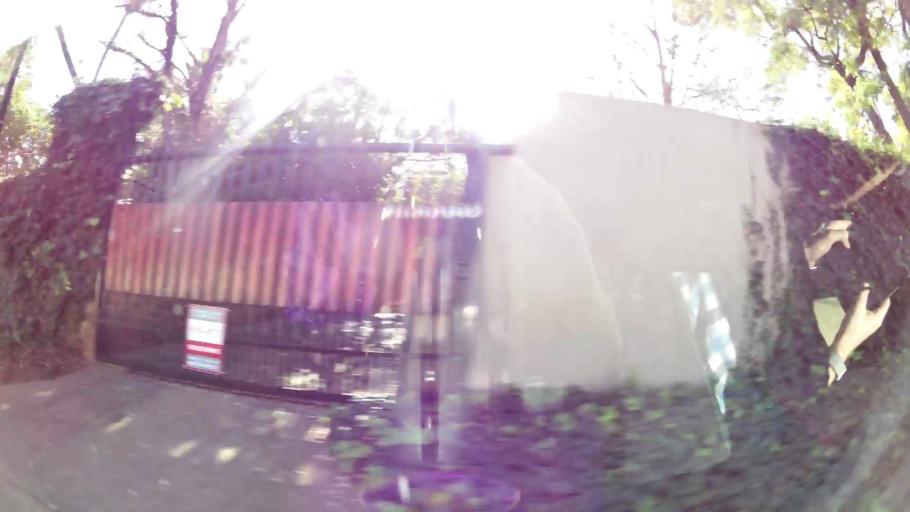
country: ZA
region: Gauteng
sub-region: City of Tshwane Metropolitan Municipality
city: Pretoria
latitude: -25.7419
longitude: 28.2178
